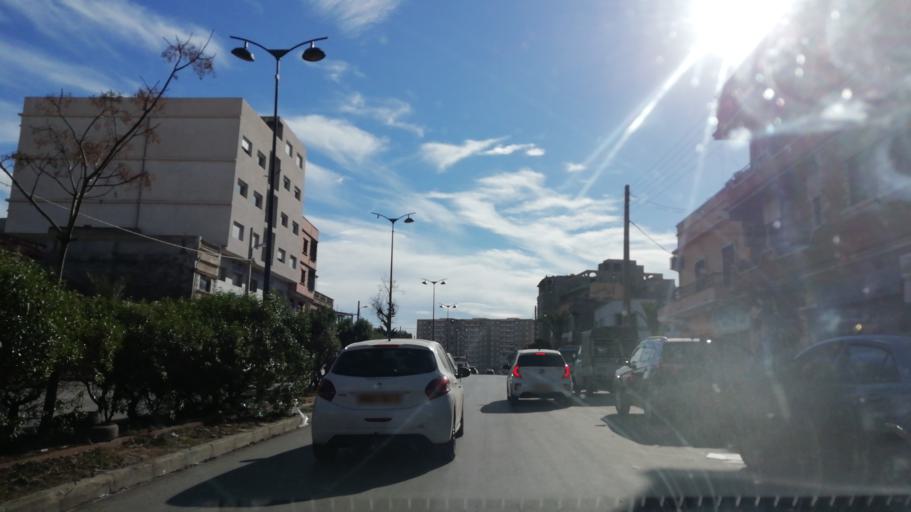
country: DZ
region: Oran
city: Oran
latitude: 35.6926
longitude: -0.6205
